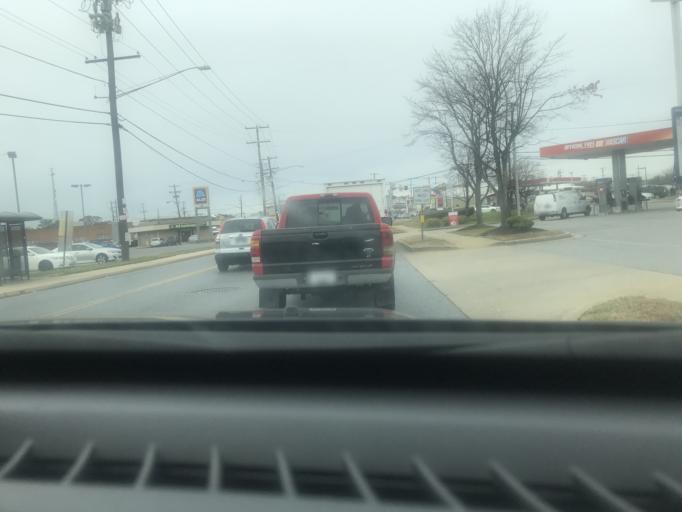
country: US
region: Maryland
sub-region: Prince George's County
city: Oxon Hill
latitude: 38.8027
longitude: -76.9886
